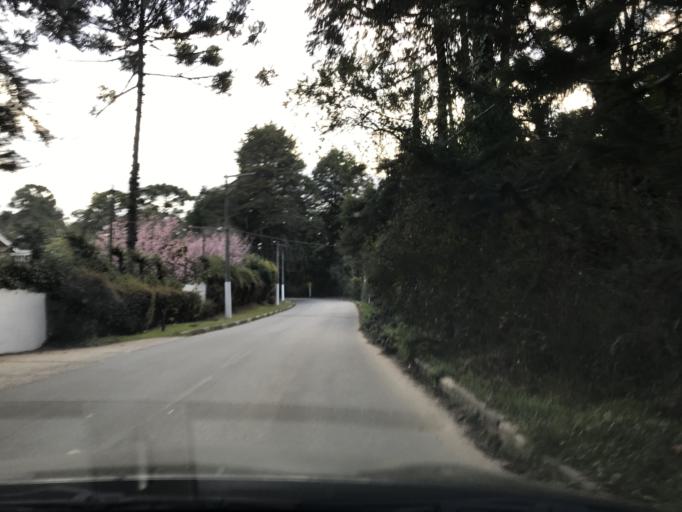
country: BR
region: Sao Paulo
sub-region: Campos Do Jordao
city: Campos do Jordao
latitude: -22.7102
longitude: -45.5492
